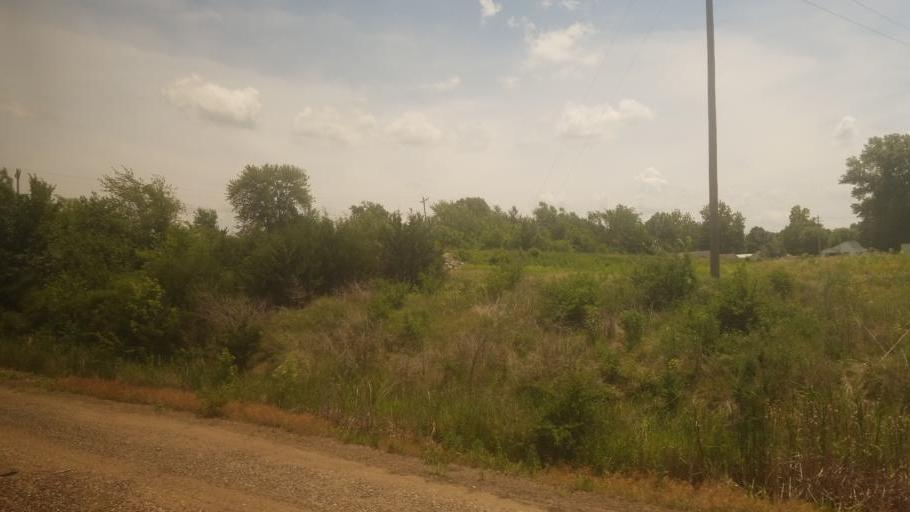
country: US
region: Missouri
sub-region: Macon County
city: La Plata
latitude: 40.0299
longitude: -92.4894
